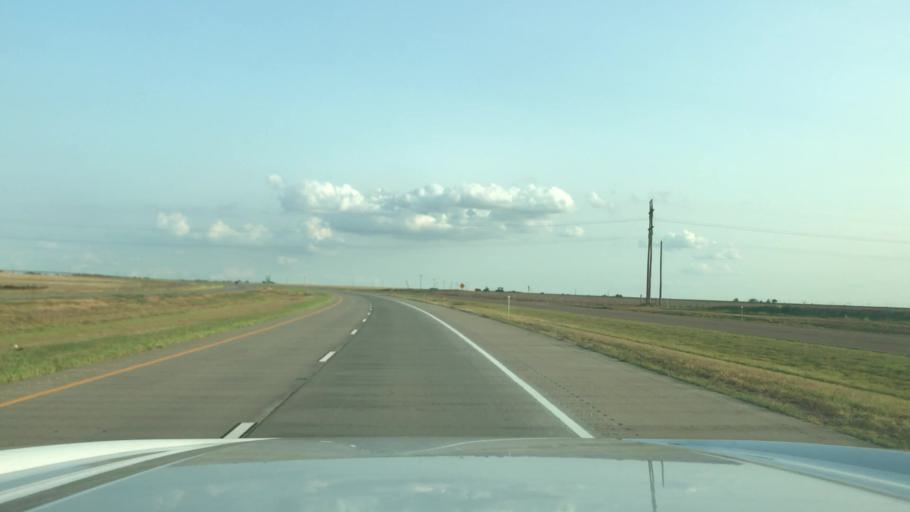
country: US
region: Texas
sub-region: Swisher County
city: Tulia
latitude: 34.3852
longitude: -101.7771
